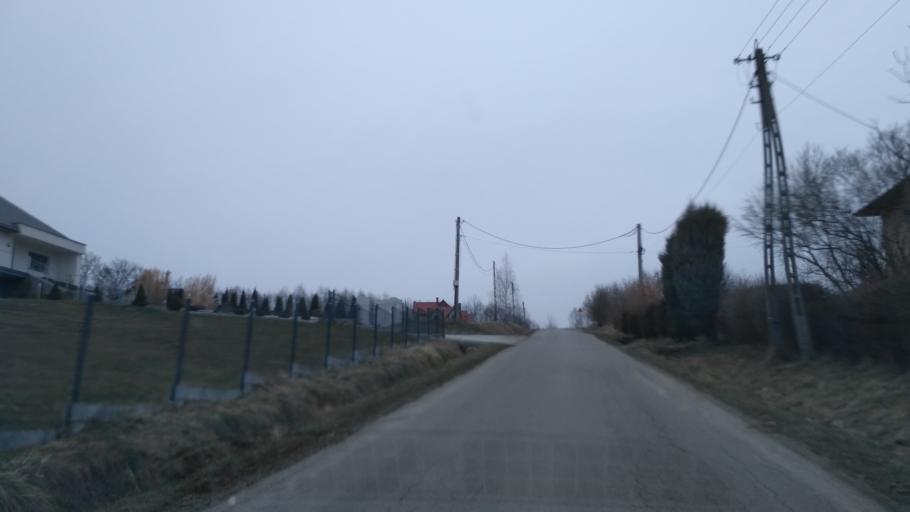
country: PL
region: Subcarpathian Voivodeship
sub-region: Powiat rzeszowski
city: Chmielnik
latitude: 49.9792
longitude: 22.1463
